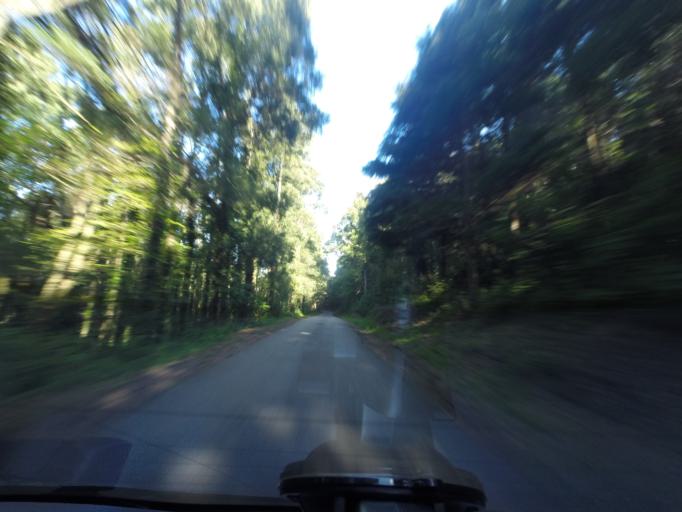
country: PT
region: Lisbon
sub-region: Sintra
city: Colares
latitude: 38.7762
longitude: -9.4670
